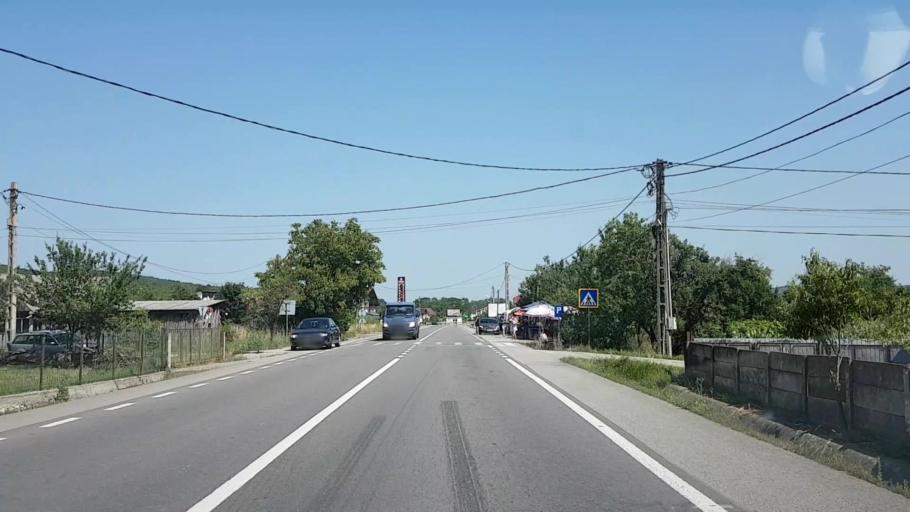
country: RO
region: Bistrita-Nasaud
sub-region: Comuna Uriu
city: Cristestii Ciceului
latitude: 47.1827
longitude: 24.1339
